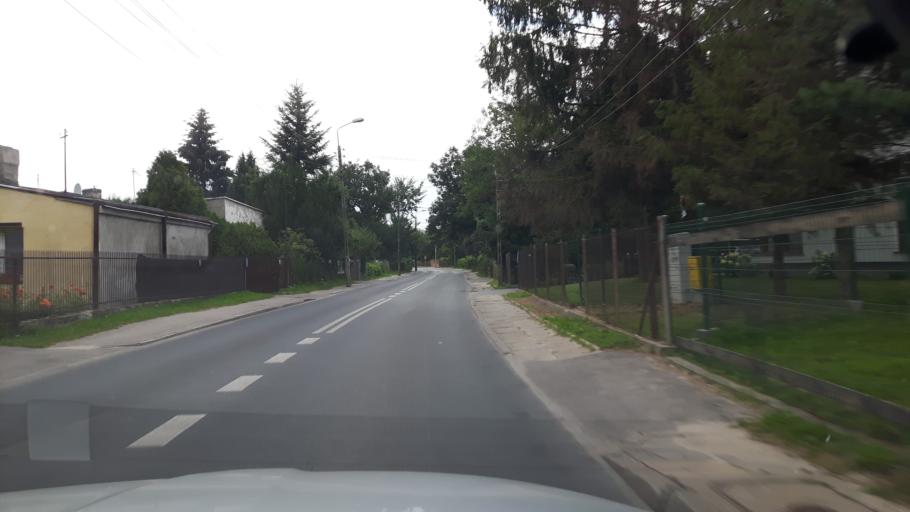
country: PL
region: Masovian Voivodeship
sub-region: Warszawa
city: Praga Poludnie
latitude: 52.2098
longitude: 21.0761
